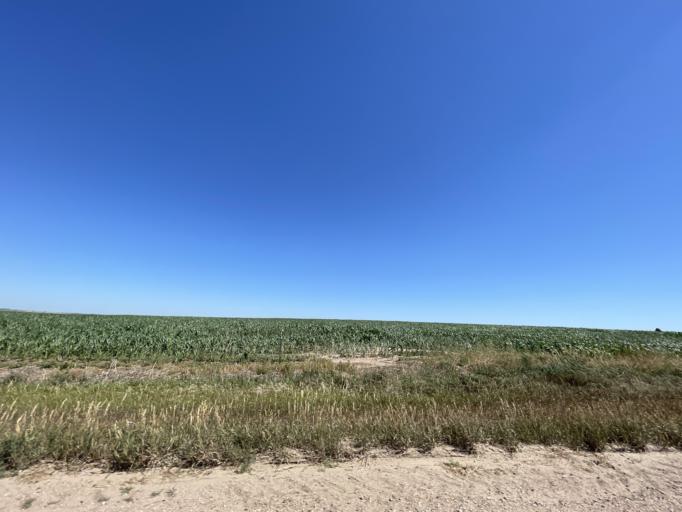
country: US
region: Nebraska
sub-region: Red Willow County
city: McCook
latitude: 40.4373
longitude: -100.6530
